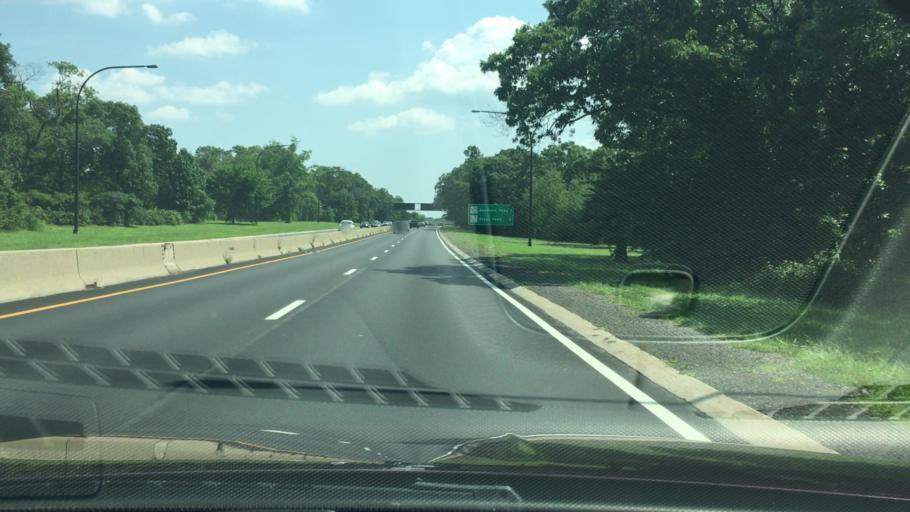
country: US
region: New York
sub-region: Nassau County
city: Levittown
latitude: 40.7142
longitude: -73.5303
